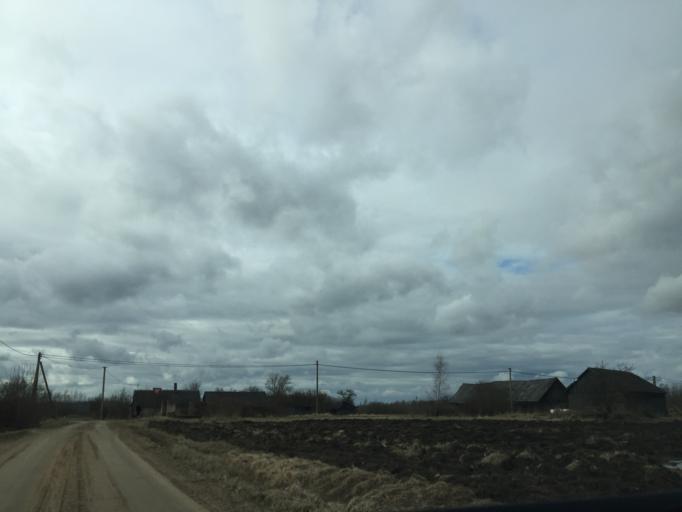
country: LV
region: Daugavpils
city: Daugavpils
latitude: 55.9486
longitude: 26.6991
